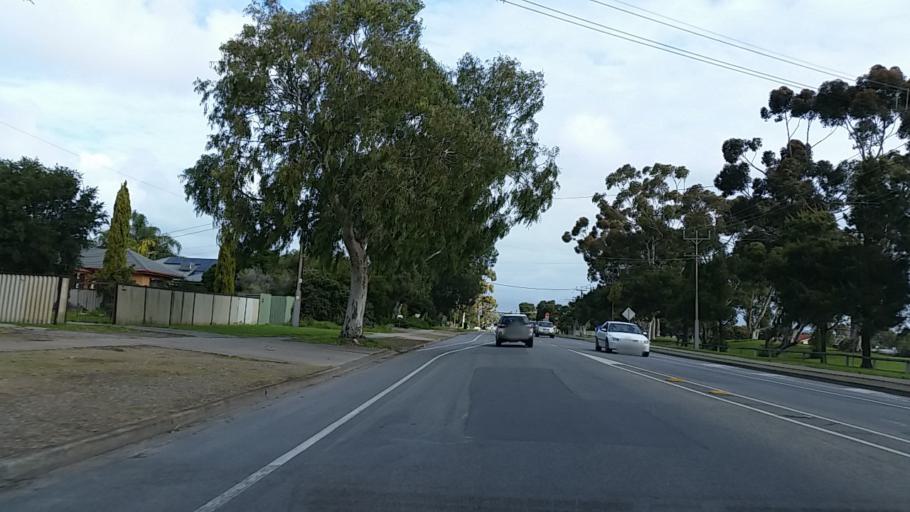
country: AU
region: South Australia
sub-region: Onkaparinga
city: Morphett Vale
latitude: -35.1270
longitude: 138.5365
